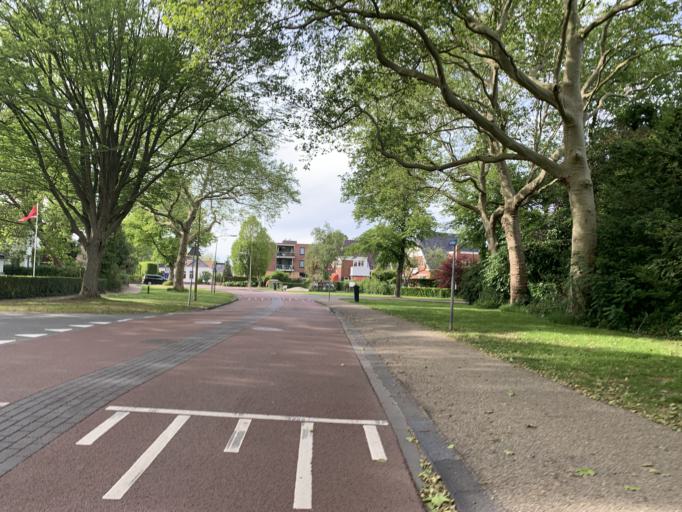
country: NL
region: Groningen
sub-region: Gemeente Haren
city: Haren
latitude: 53.1724
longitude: 6.6105
